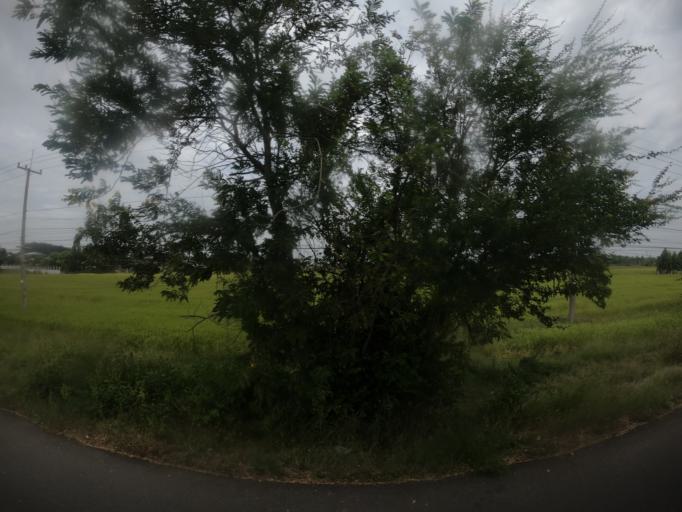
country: TH
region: Kalasin
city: Khong Chai
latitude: 16.1378
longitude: 103.4396
